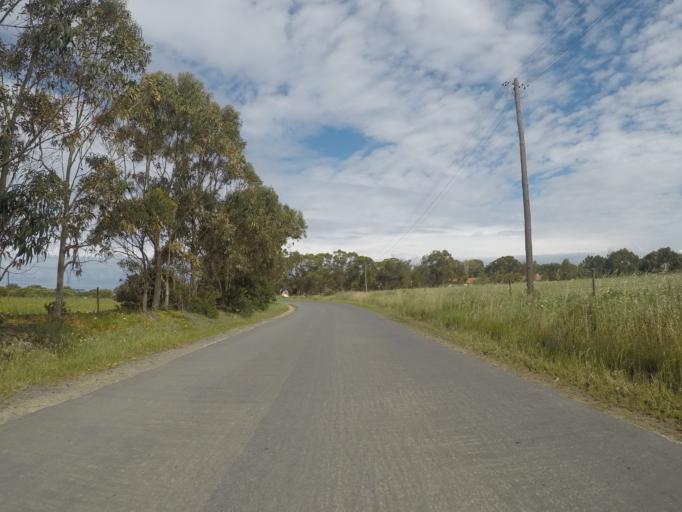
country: PT
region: Beja
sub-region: Odemira
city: Sao Teotonio
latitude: 37.4940
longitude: -8.7845
